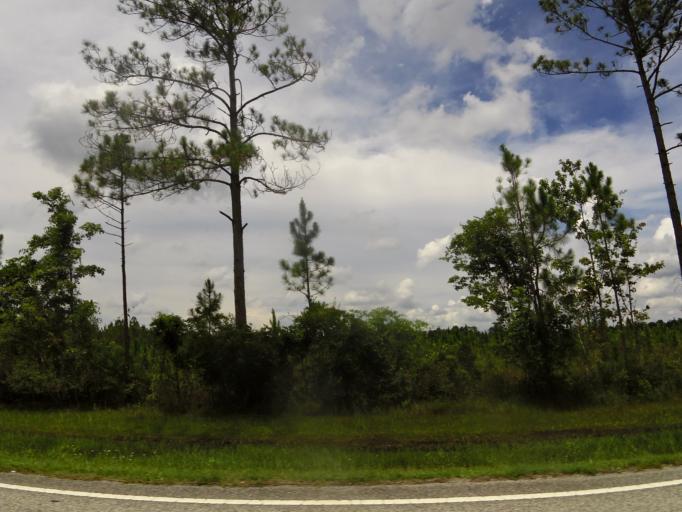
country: US
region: Florida
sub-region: Saint Johns County
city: Saint Augustine Shores
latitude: 29.6520
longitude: -81.3772
